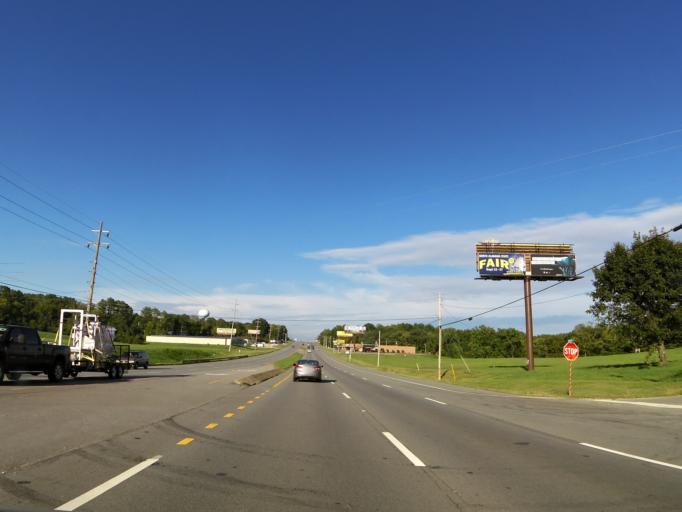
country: US
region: Alabama
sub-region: Lauderdale County
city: East Florence
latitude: 34.8332
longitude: -87.6146
